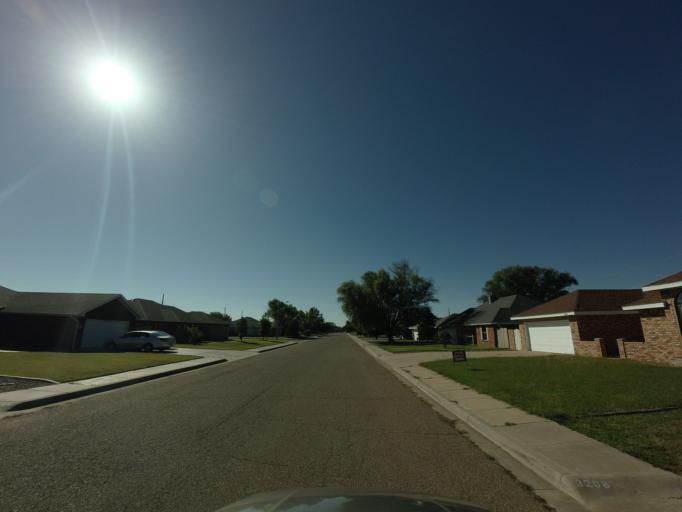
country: US
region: New Mexico
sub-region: Curry County
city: Clovis
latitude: 34.4330
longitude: -103.2268
